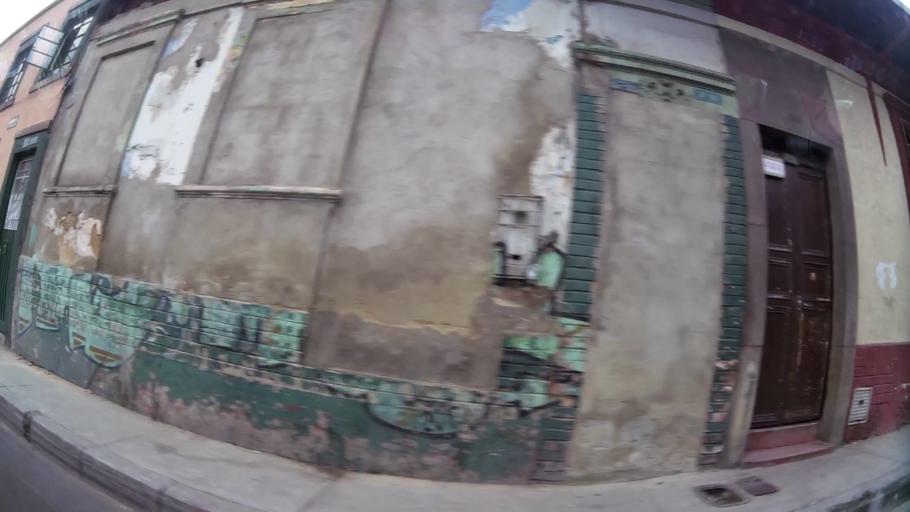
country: CO
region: Bogota D.C.
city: Bogota
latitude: 4.5901
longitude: -74.0788
